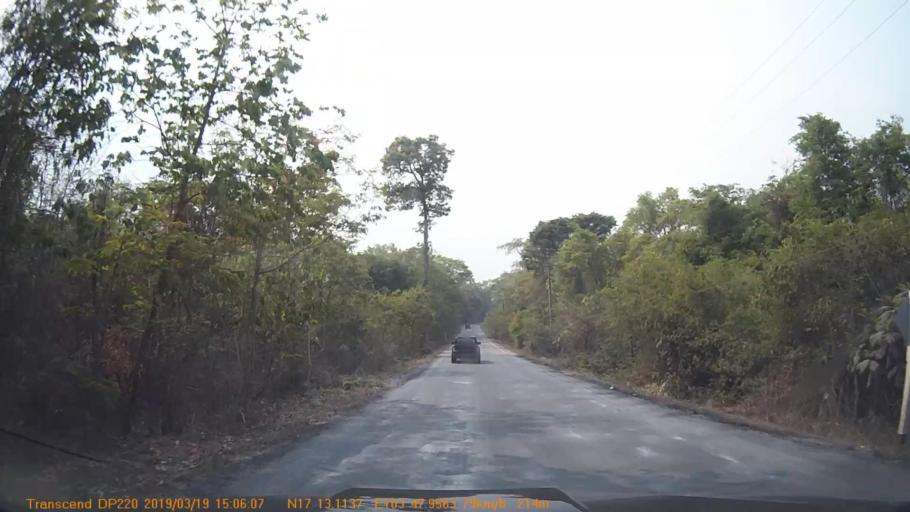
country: TH
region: Sakon Nakhon
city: Nikhom Nam Un
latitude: 17.2187
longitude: 103.7991
